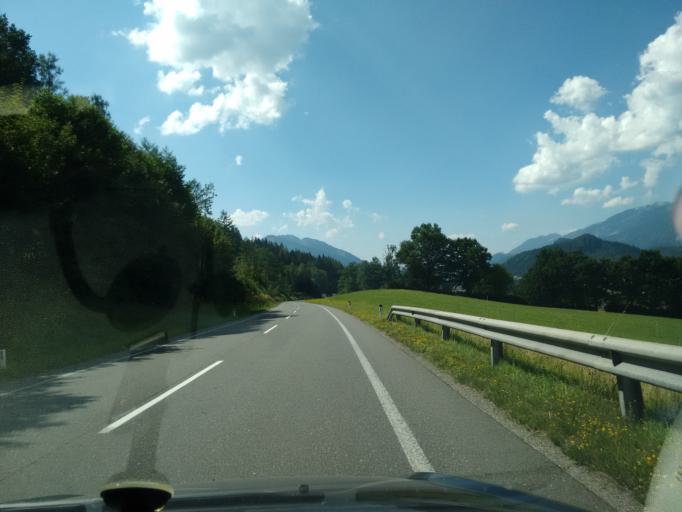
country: AT
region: Upper Austria
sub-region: Politischer Bezirk Kirchdorf an der Krems
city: Rossleithen
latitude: 47.7117
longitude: 14.3352
